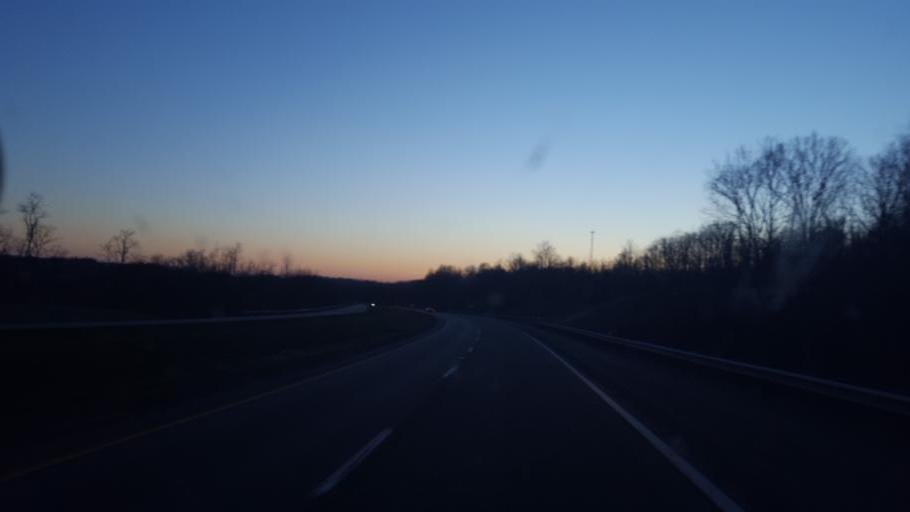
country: US
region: Ohio
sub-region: Belmont County
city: Bethesda
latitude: 40.0603
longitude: -81.1021
